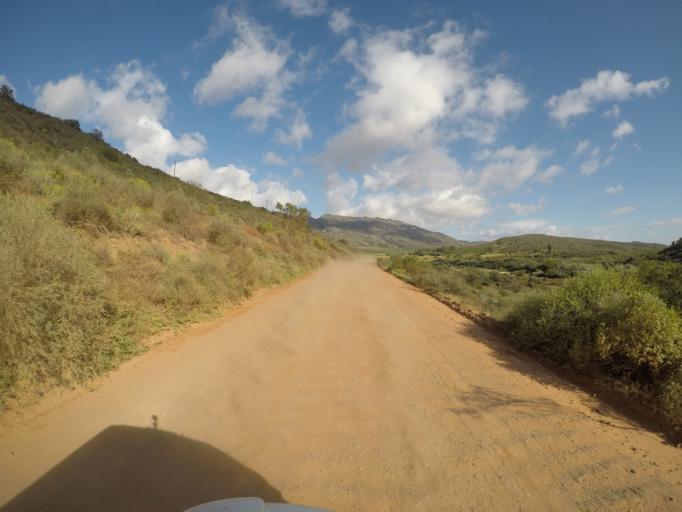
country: ZA
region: Western Cape
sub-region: West Coast District Municipality
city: Clanwilliam
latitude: -32.3642
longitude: 18.9473
